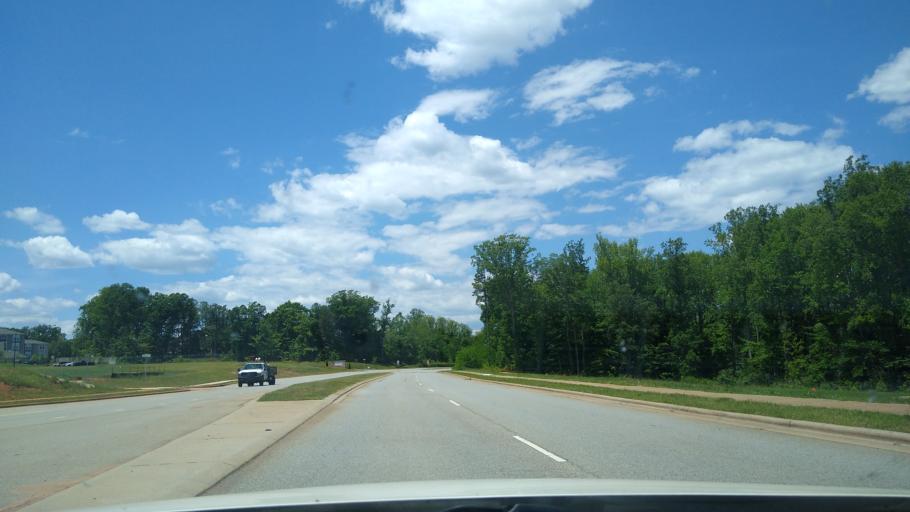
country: US
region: North Carolina
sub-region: Guilford County
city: Jamestown
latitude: 36.0668
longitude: -79.9052
